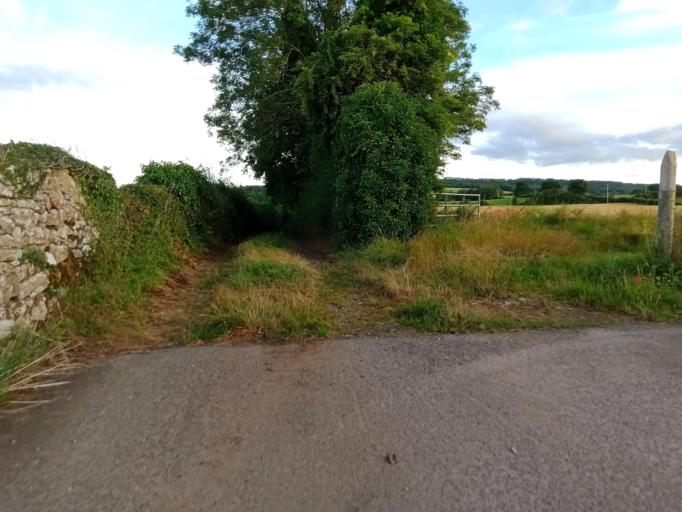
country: IE
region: Leinster
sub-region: Laois
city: Abbeyleix
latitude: 52.8409
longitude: -7.4003
